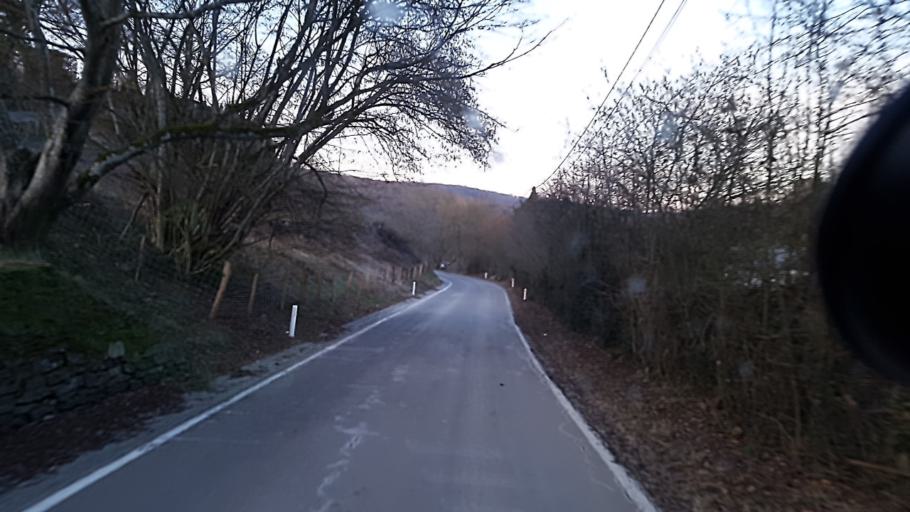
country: BE
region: Wallonia
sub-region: Province du Luxembourg
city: Daverdisse
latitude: 50.0234
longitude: 5.1164
